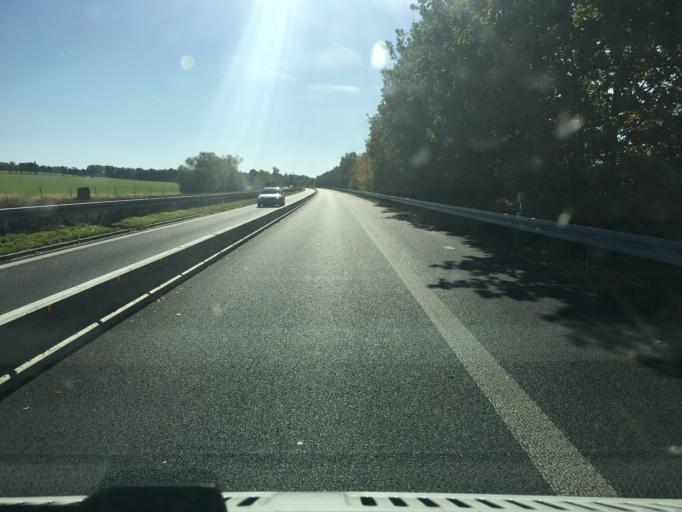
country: DE
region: Saxony
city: Zwickau
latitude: 50.7527
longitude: 12.5019
